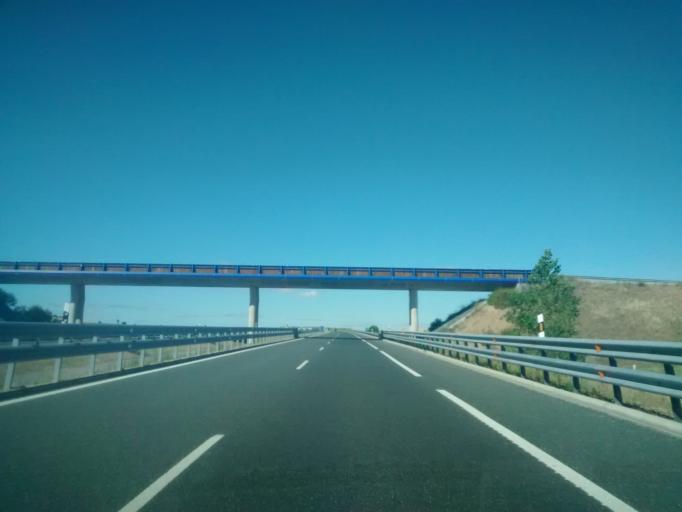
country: ES
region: Castille and Leon
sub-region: Provincia de Avila
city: Munosancho
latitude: 40.8871
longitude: -5.0290
